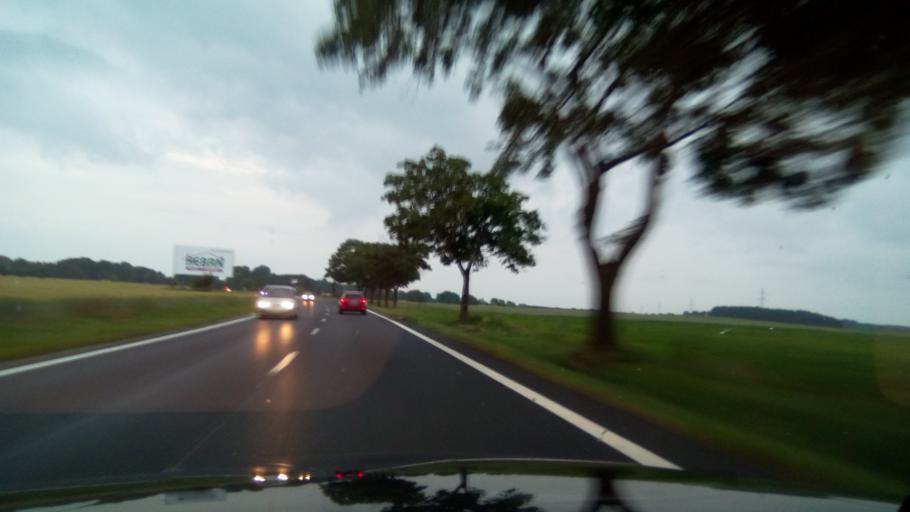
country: PL
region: Greater Poland Voivodeship
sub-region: Powiat poznanski
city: Pobiedziska
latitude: 52.4975
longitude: 17.3391
